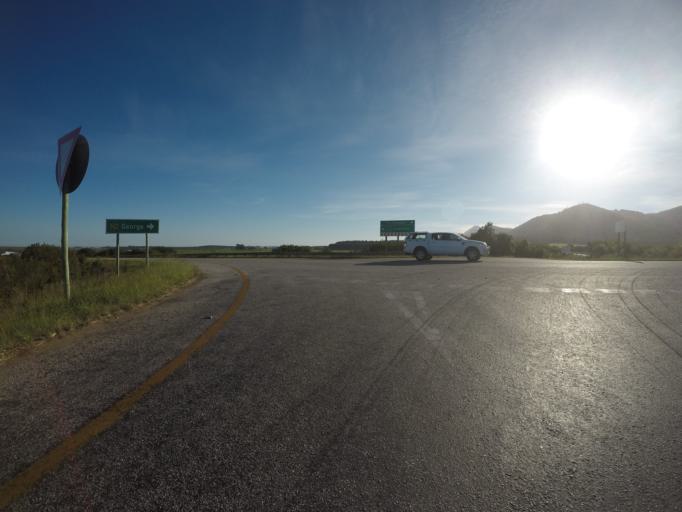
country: ZA
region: Eastern Cape
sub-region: Cacadu District Municipality
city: Kareedouw
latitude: -33.9998
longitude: 24.2355
